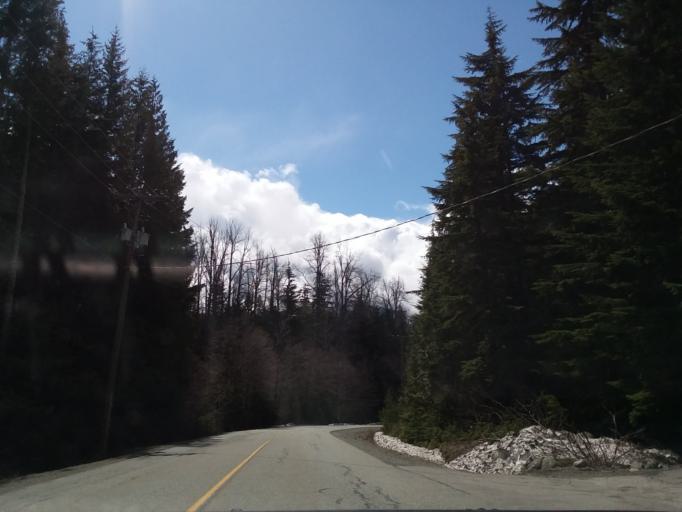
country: CA
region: British Columbia
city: Whistler
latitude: 50.1281
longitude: -122.9862
